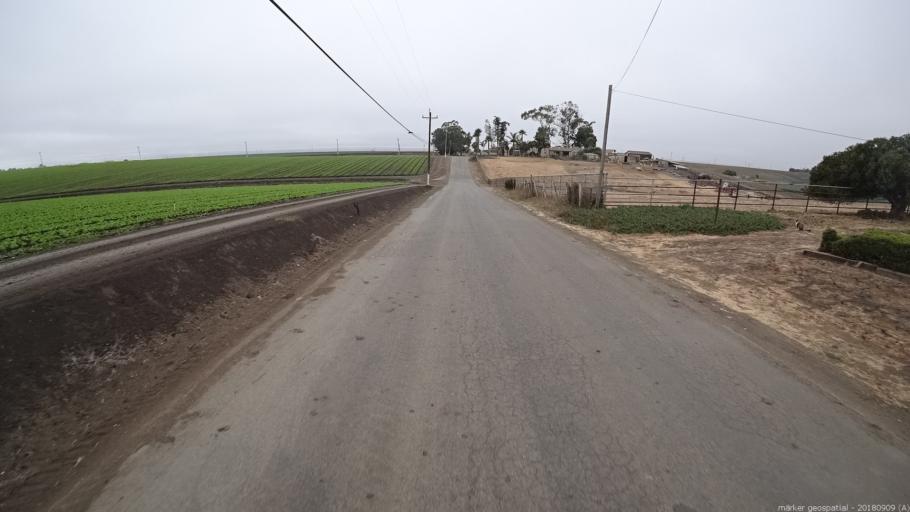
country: US
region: California
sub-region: Monterey County
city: Boronda
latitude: 36.7198
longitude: -121.6817
